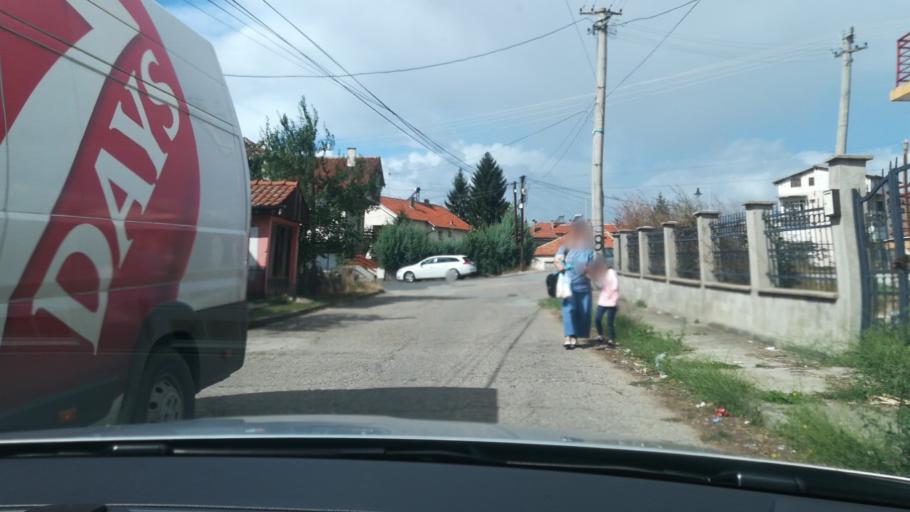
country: MK
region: Delcevo
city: Delcevo
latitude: 41.9651
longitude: 22.7762
